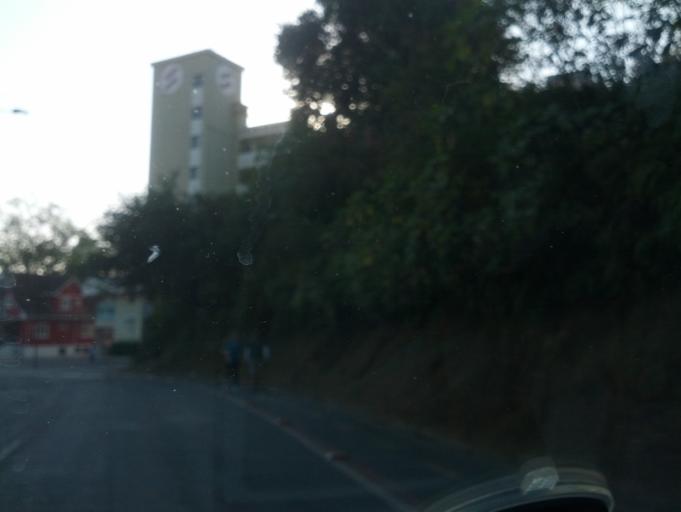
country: BR
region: Santa Catarina
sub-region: Blumenau
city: Blumenau
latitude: -26.9115
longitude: -49.0850
